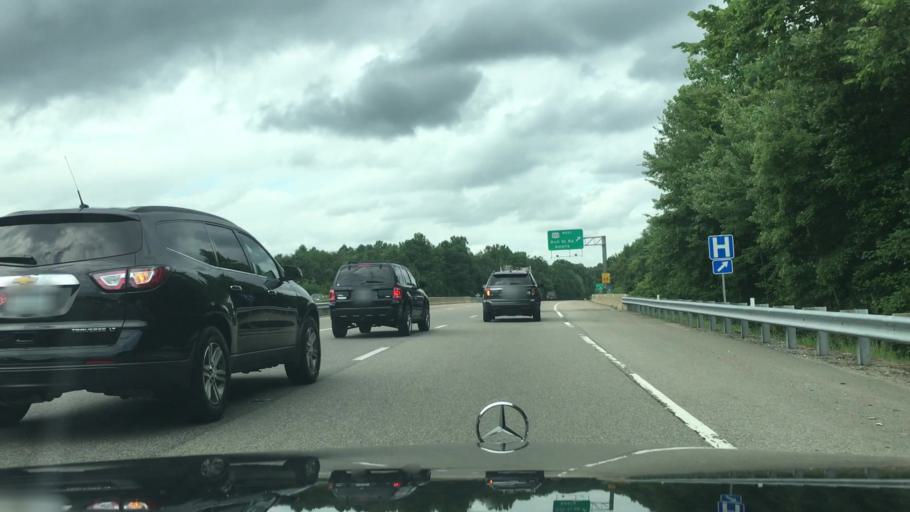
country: US
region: Virginia
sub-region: Chesterfield County
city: Brandermill
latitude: 37.4231
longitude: -77.6297
